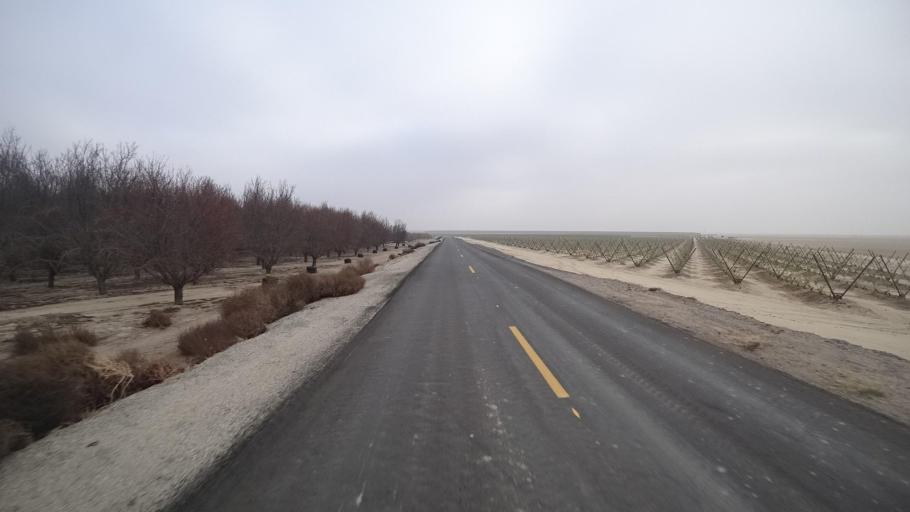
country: US
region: California
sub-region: Kern County
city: Maricopa
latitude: 35.1200
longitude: -119.3583
